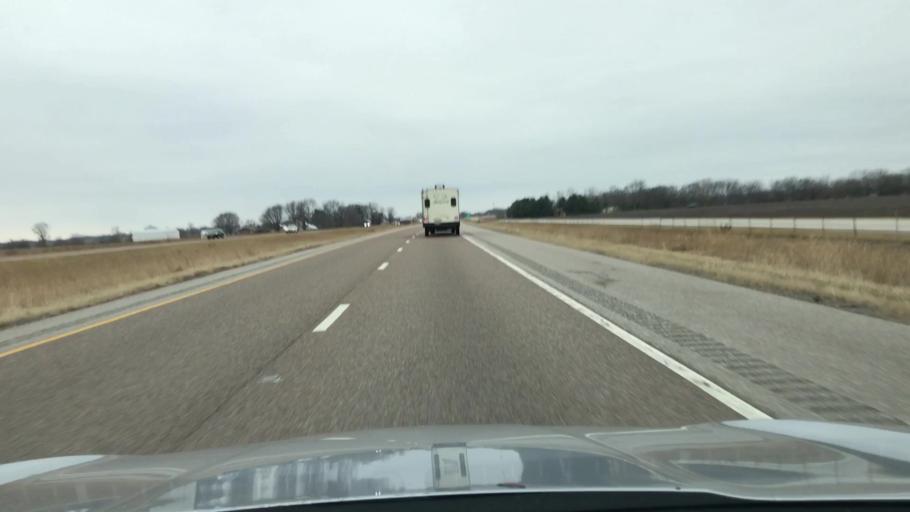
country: US
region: Illinois
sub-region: Madison County
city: Worden
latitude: 38.9425
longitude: -89.7869
